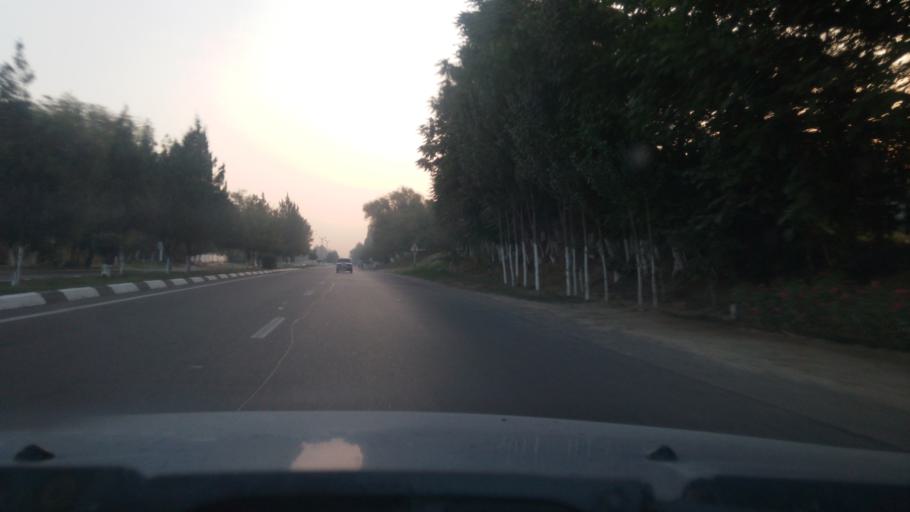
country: UZ
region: Toshkent
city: Amir Timur
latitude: 41.0654
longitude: 68.9167
